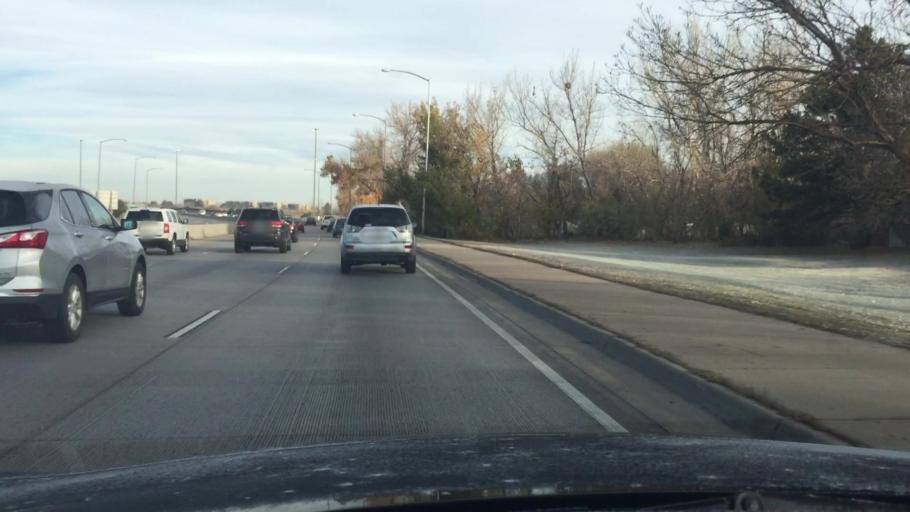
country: US
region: Colorado
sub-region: Arapahoe County
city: Dove Valley
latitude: 39.6481
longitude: -104.8288
